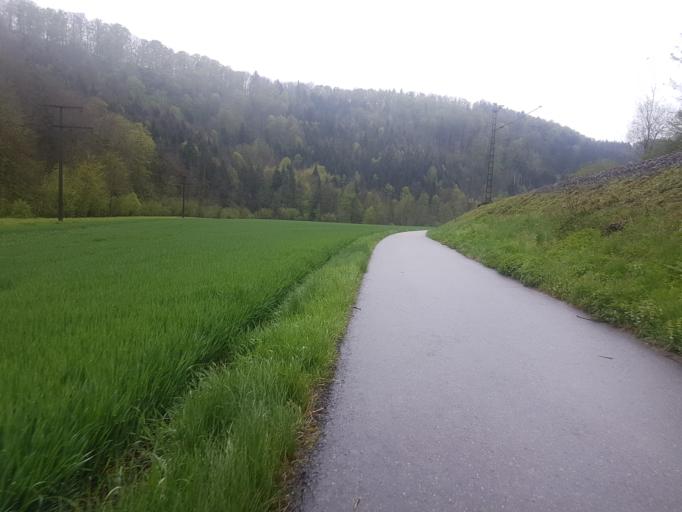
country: DE
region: Baden-Wuerttemberg
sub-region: Freiburg Region
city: Epfendorf
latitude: 48.2296
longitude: 8.6103
